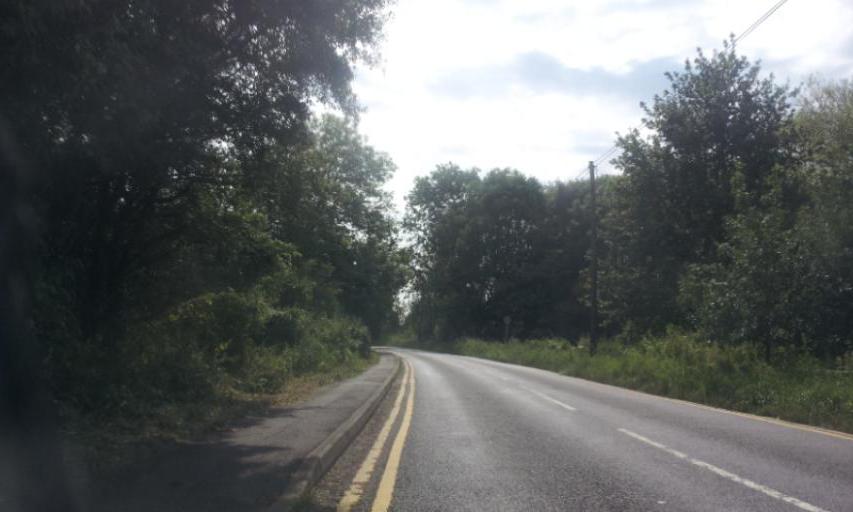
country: GB
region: England
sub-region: Kent
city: Yalding
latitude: 51.2194
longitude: 0.4210
